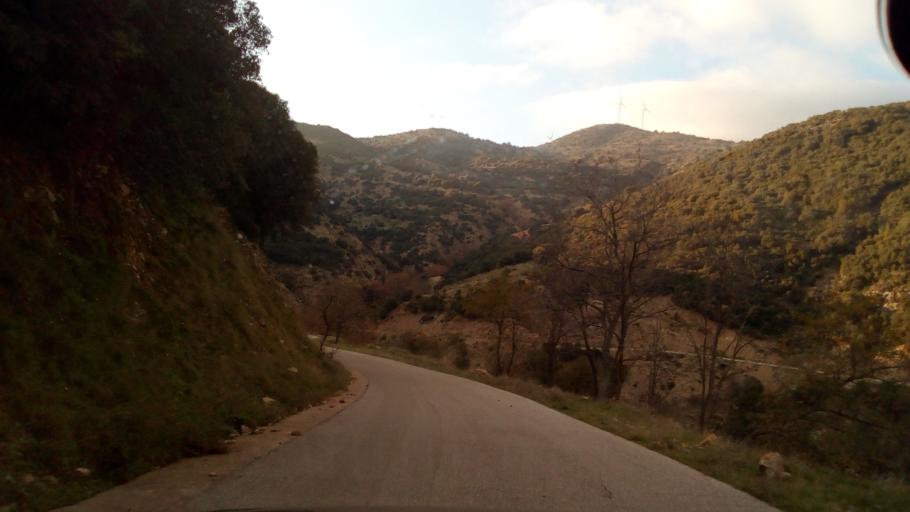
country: GR
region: West Greece
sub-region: Nomos Aitolias kai Akarnanias
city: Nafpaktos
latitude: 38.4235
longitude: 21.8186
